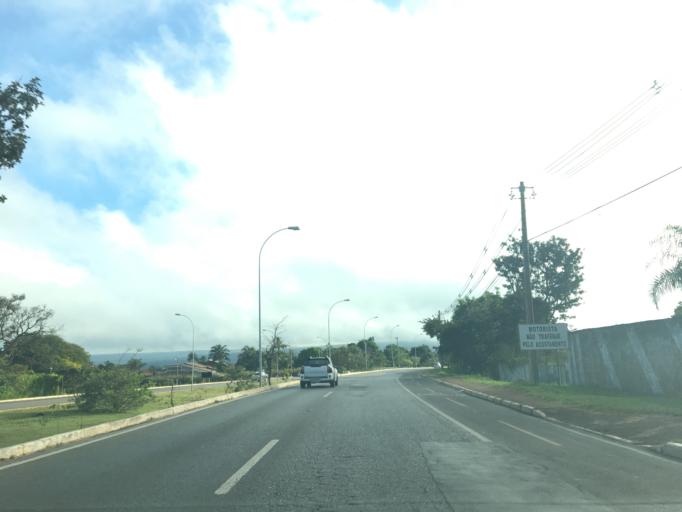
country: BR
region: Federal District
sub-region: Brasilia
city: Brasilia
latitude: -15.8148
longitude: -47.8059
